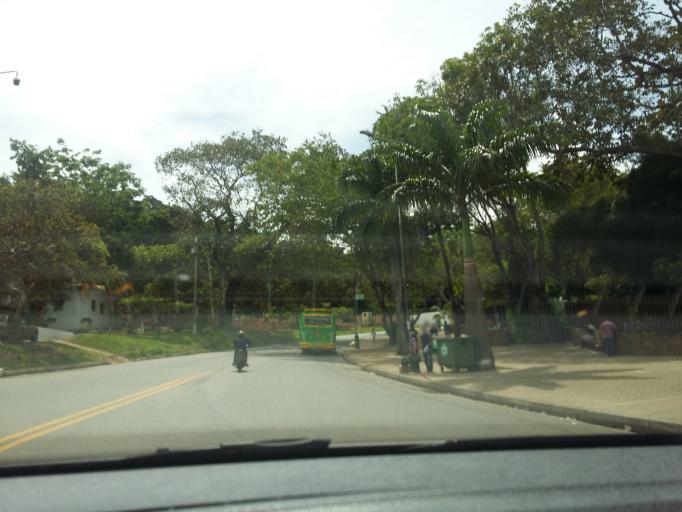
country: CO
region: Santander
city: Bucaramanga
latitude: 7.1312
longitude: -73.1101
